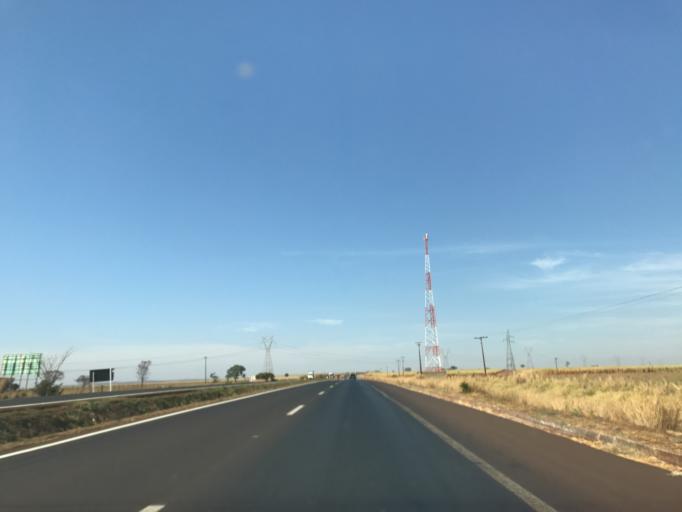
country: BR
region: Minas Gerais
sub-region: Centralina
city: Centralina
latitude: -18.5008
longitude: -49.1890
